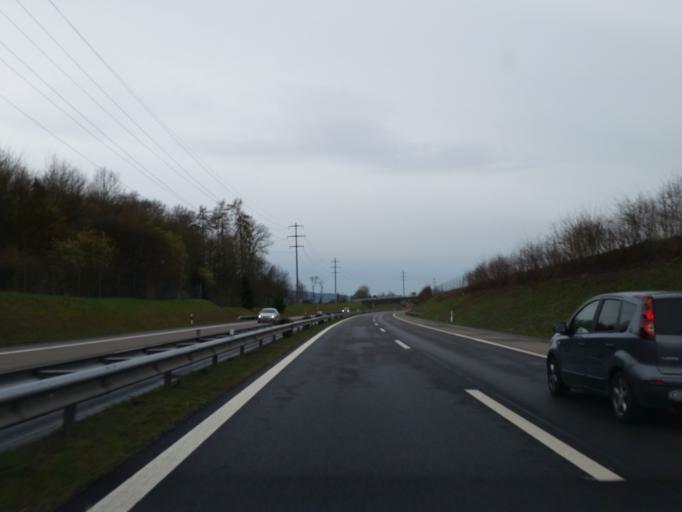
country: CH
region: Thurgau
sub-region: Weinfelden District
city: Maerstetten-Dorf
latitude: 47.6142
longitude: 9.1019
